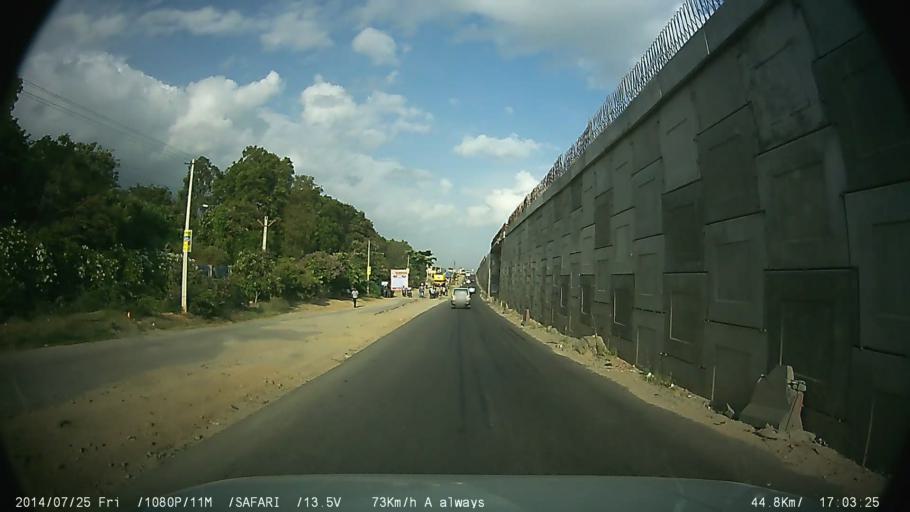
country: IN
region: Tamil Nadu
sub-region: Krishnagiri
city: Hosur
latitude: 12.7175
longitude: 77.8769
